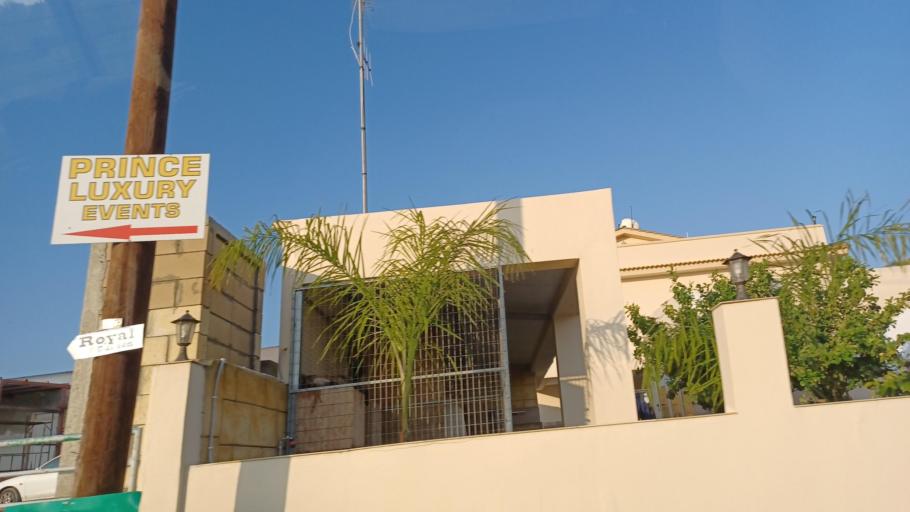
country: CY
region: Lefkosia
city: Lympia
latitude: 34.9932
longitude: 33.4646
